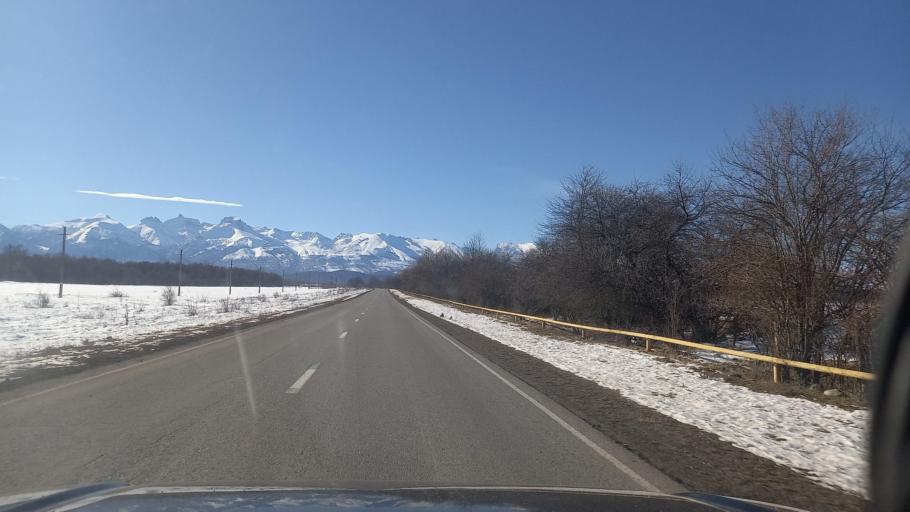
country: RU
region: North Ossetia
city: Chikola
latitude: 43.1766
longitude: 43.8795
